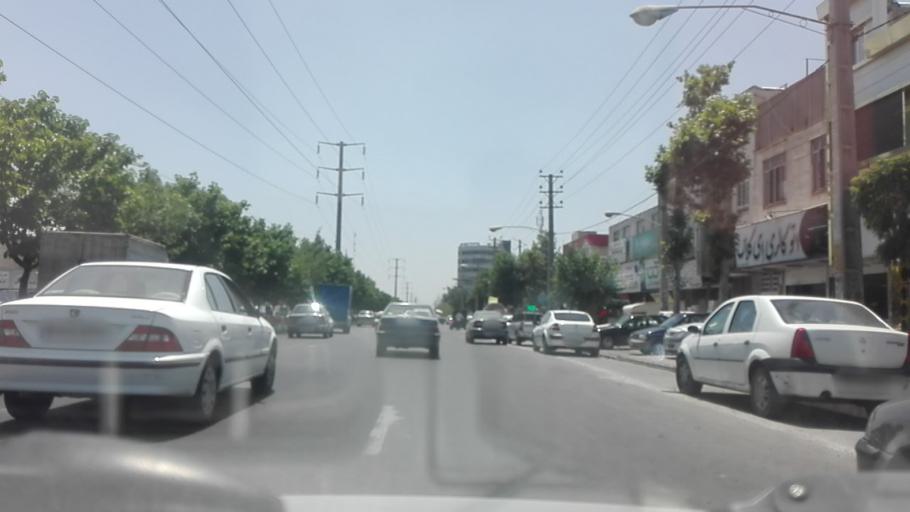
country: IR
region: Tehran
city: Shahre Jadide Andisheh
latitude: 35.7175
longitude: 50.9933
